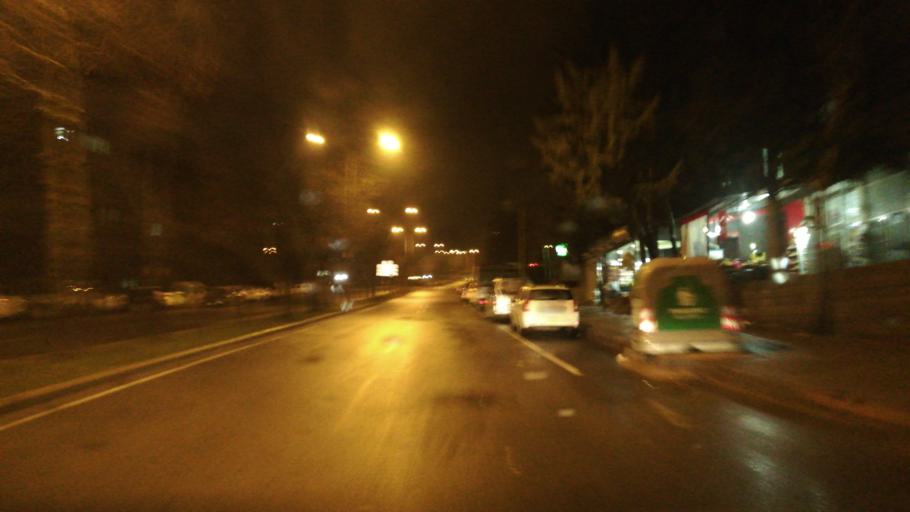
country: TR
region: Kahramanmaras
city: Kahramanmaras
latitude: 37.5942
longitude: 36.8687
